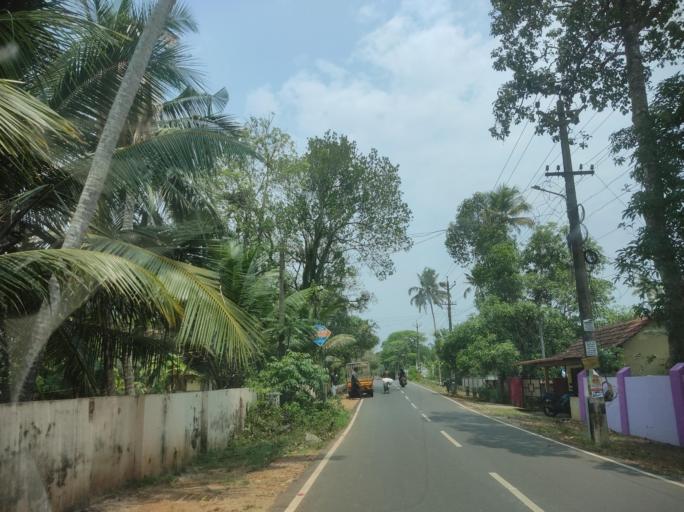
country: IN
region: Kerala
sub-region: Alappuzha
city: Vayalar
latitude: 9.7051
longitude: 76.3256
